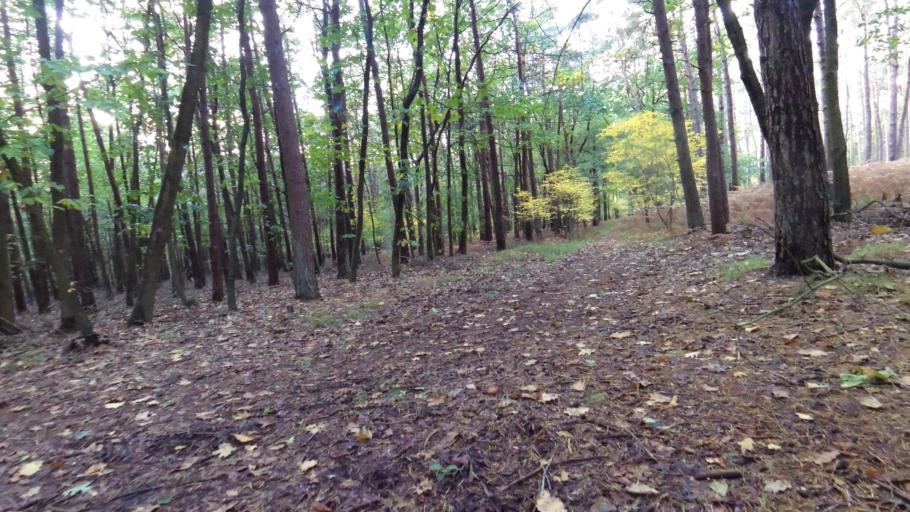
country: NL
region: Utrecht
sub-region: Gemeente Soest
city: Soest
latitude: 52.1856
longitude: 5.2579
